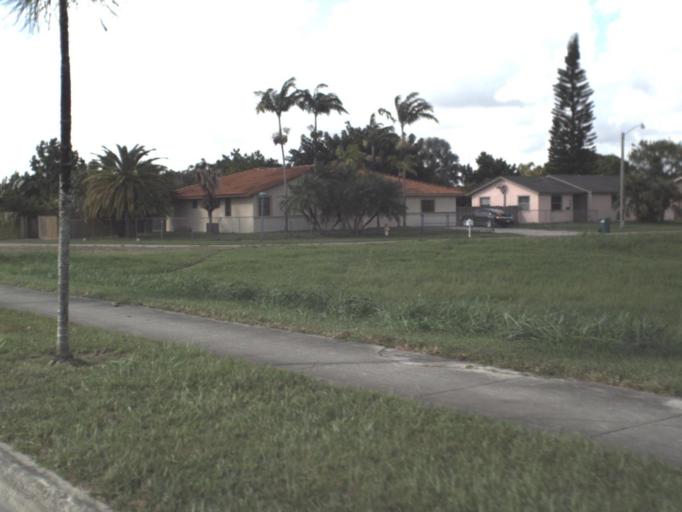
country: US
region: Florida
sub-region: Miami-Dade County
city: Leisure City
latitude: 25.4997
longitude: -80.4200
